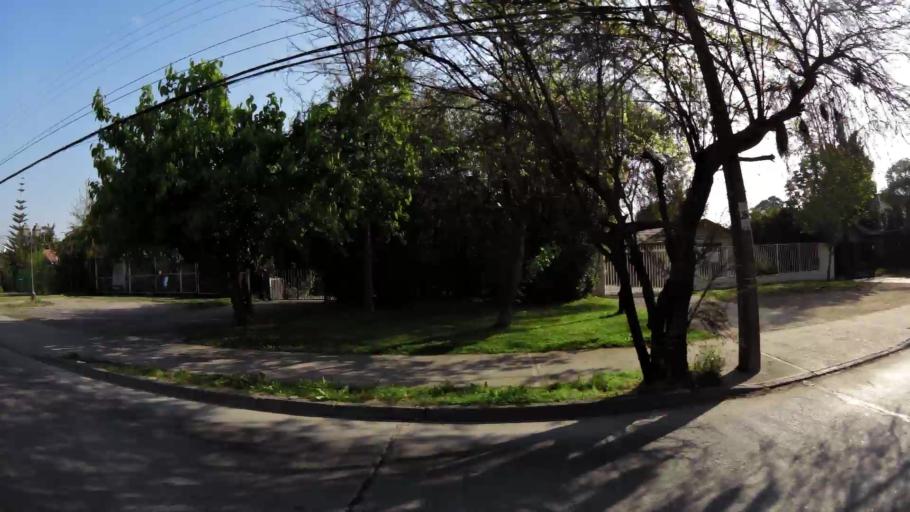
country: CL
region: Santiago Metropolitan
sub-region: Provincia de Santiago
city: Villa Presidente Frei, Nunoa, Santiago, Chile
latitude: -33.3806
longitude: -70.5532
